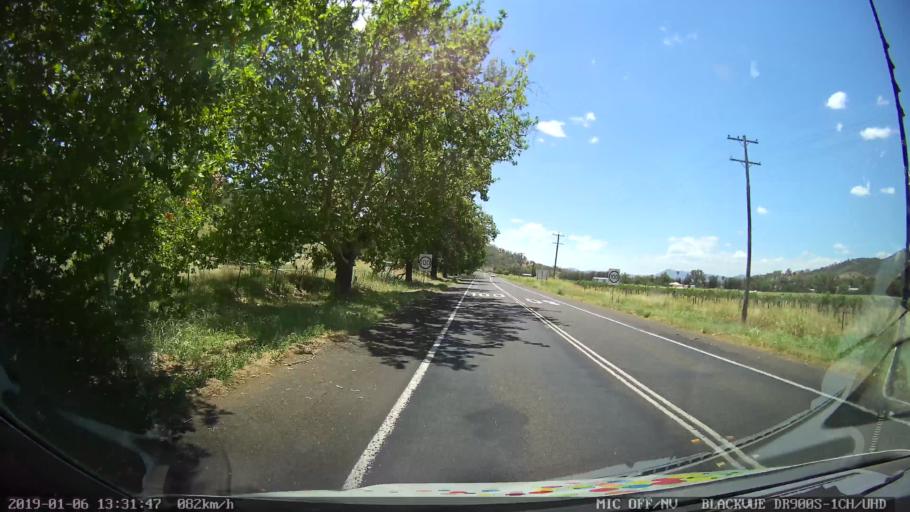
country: AU
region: New South Wales
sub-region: Tamworth Municipality
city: East Tamworth
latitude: -31.1178
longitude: 150.9957
